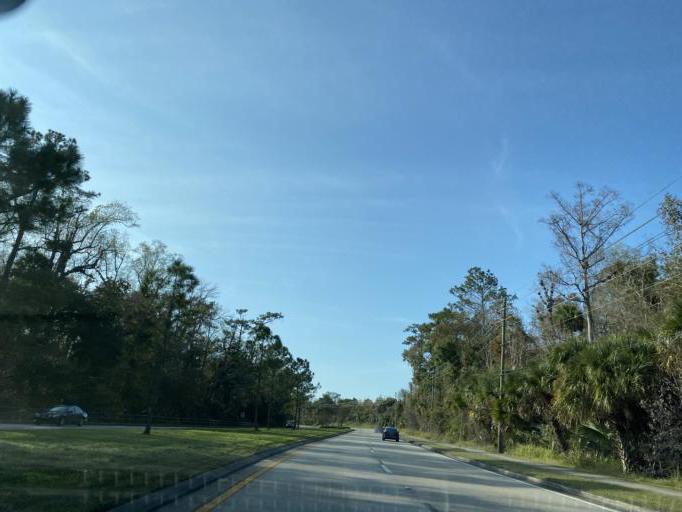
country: US
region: Florida
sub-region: Seminole County
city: Longwood
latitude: 28.7267
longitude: -81.3258
